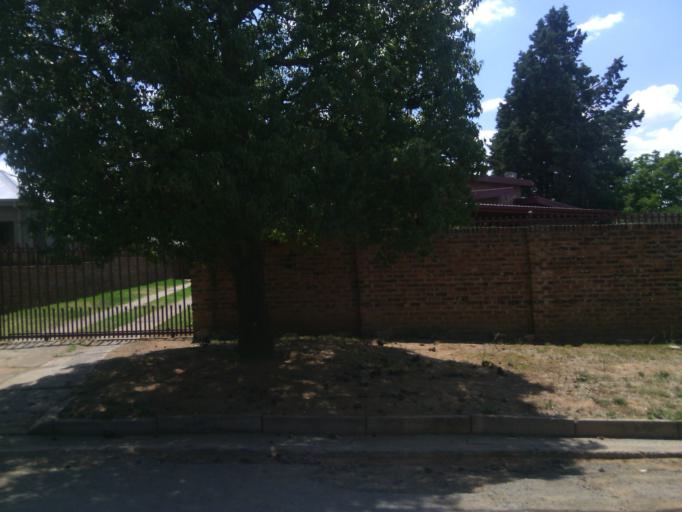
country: ZA
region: Orange Free State
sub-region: Xhariep District Municipality
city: Dewetsdorp
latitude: -29.5831
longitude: 26.6625
